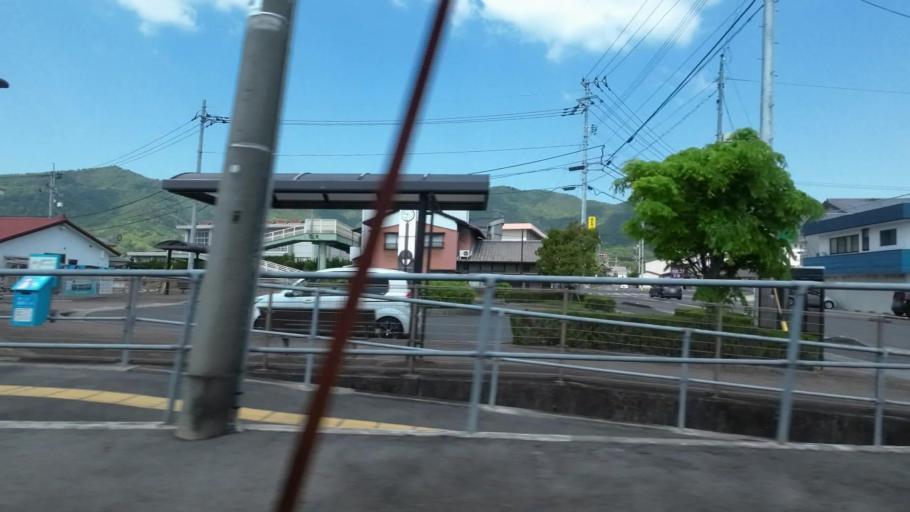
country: JP
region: Kagawa
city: Kan'onjicho
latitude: 34.1675
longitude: 133.6904
